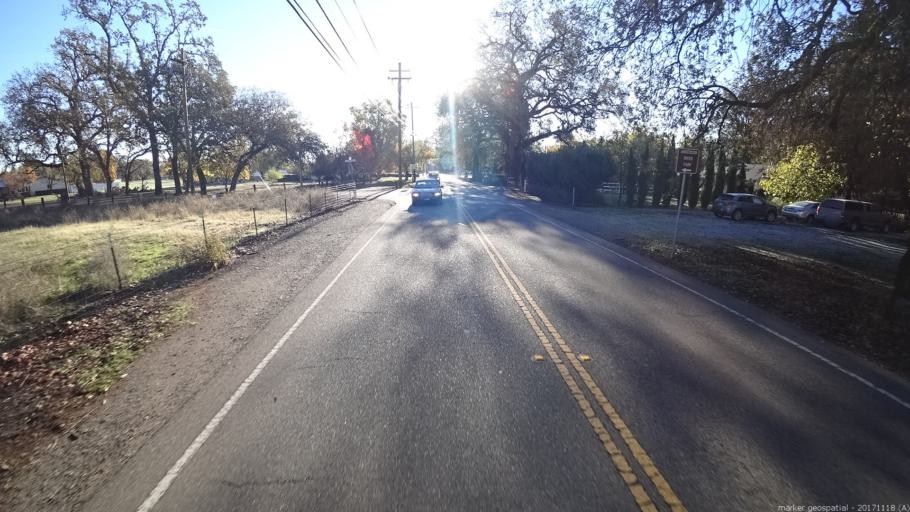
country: US
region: California
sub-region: Shasta County
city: Anderson
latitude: 40.4549
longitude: -122.2803
